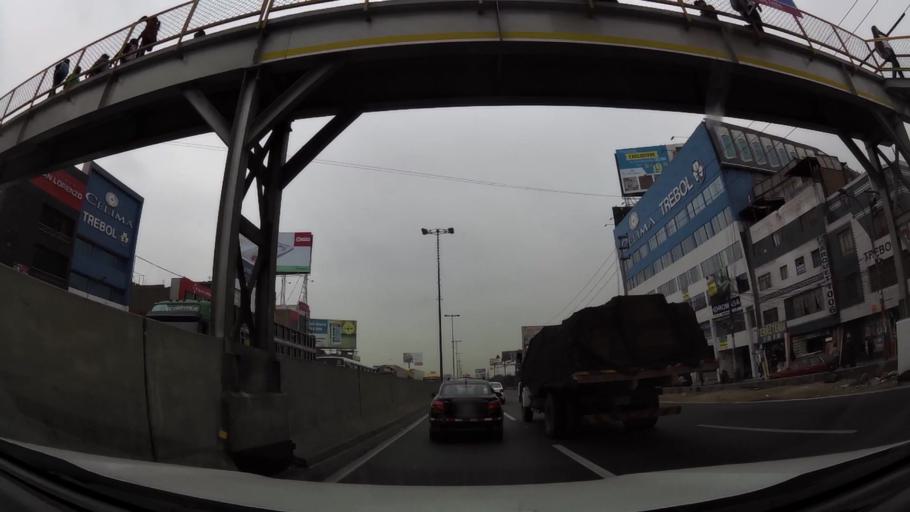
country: PE
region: Lima
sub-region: Lima
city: Independencia
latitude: -12.0185
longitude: -77.0596
